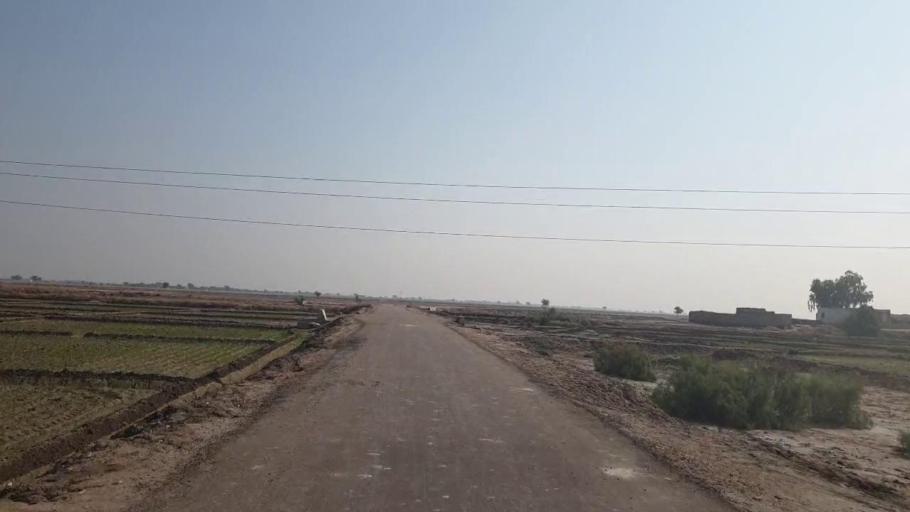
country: PK
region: Sindh
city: Bhan
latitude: 26.4370
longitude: 67.7337
